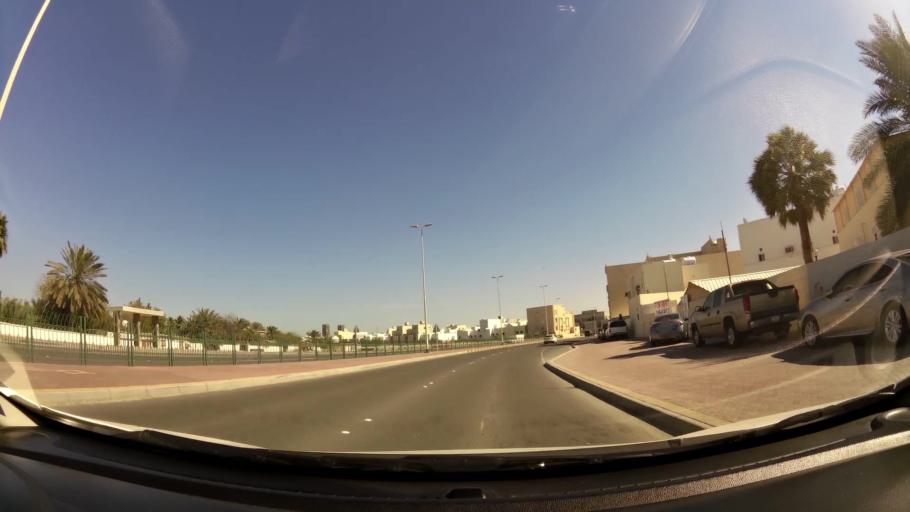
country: BH
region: Muharraq
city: Al Hadd
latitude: 26.2548
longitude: 50.6495
